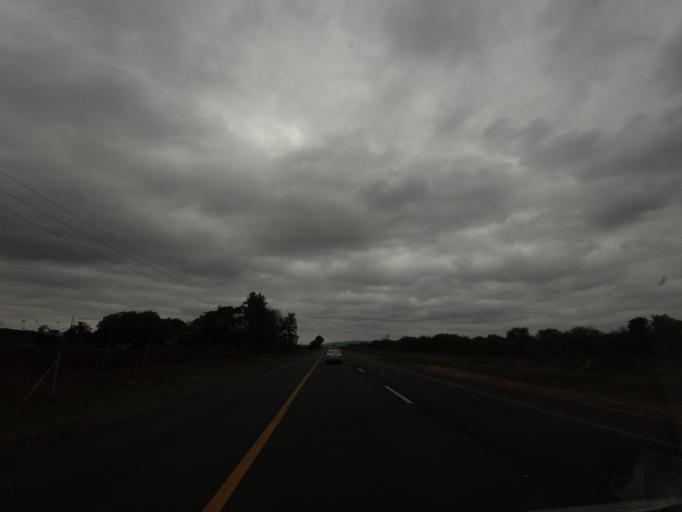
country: ZA
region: Mpumalanga
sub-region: Ehlanzeni District
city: Komatipoort
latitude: -25.4402
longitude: 31.8752
